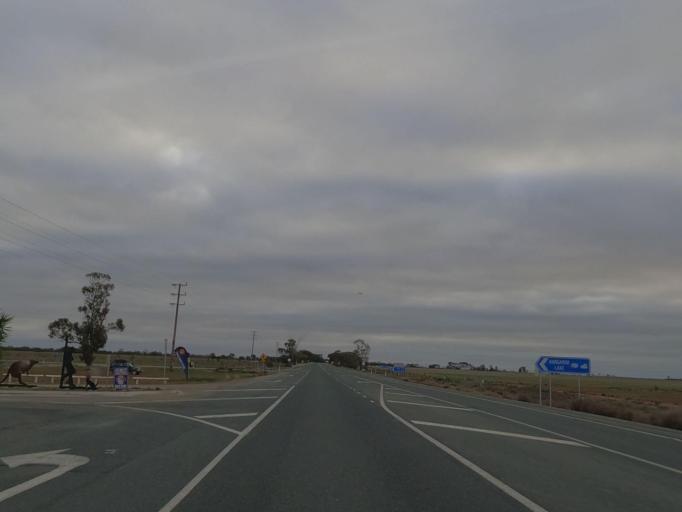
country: AU
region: Victoria
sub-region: Swan Hill
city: Swan Hill
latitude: -35.5520
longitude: 143.7710
